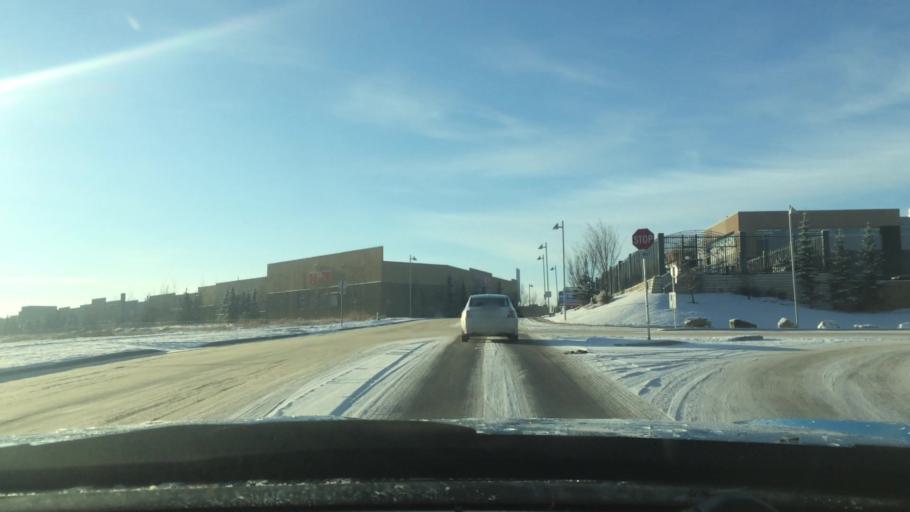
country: CA
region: Alberta
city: Calgary
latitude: 51.1605
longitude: -114.1597
